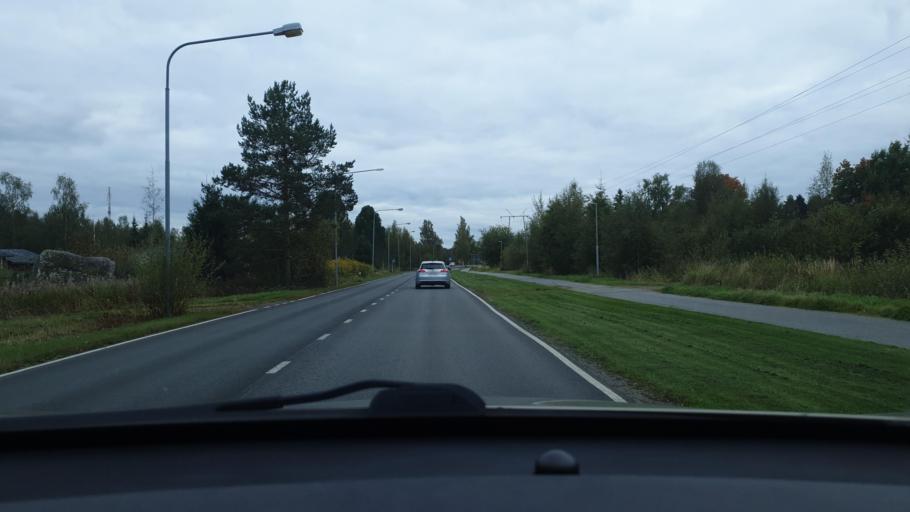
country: FI
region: Ostrobothnia
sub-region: Vaasa
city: Teeriniemi
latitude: 63.0924
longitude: 21.6983
